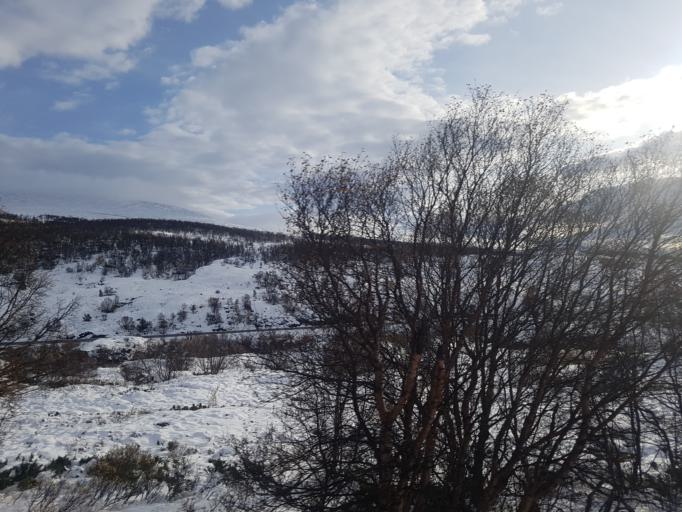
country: NO
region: Sor-Trondelag
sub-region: Oppdal
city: Oppdal
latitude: 62.2797
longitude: 9.5893
